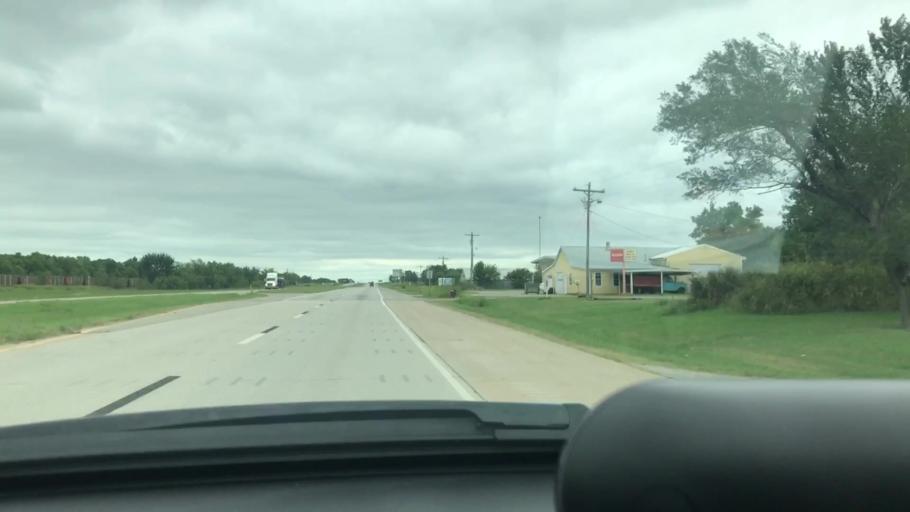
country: US
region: Oklahoma
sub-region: Mayes County
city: Chouteau
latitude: 36.0993
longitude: -95.3626
